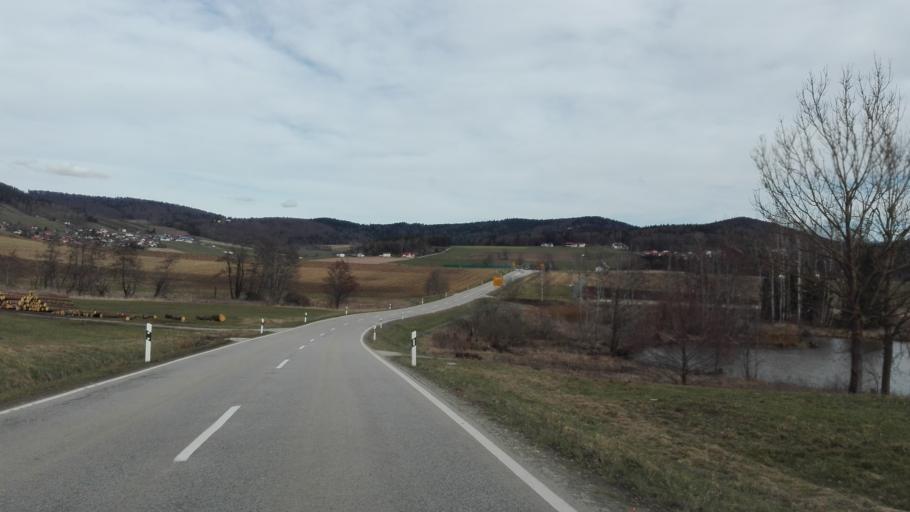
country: DE
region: Bavaria
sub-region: Lower Bavaria
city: Hauzenberg
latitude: 48.6290
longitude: 13.6493
